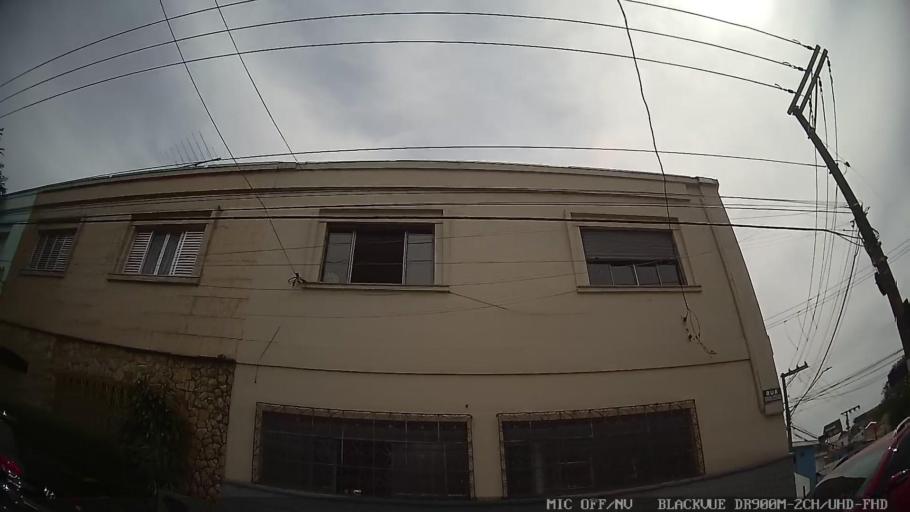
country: BR
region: Sao Paulo
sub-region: Guarulhos
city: Guarulhos
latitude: -23.5303
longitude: -46.5470
